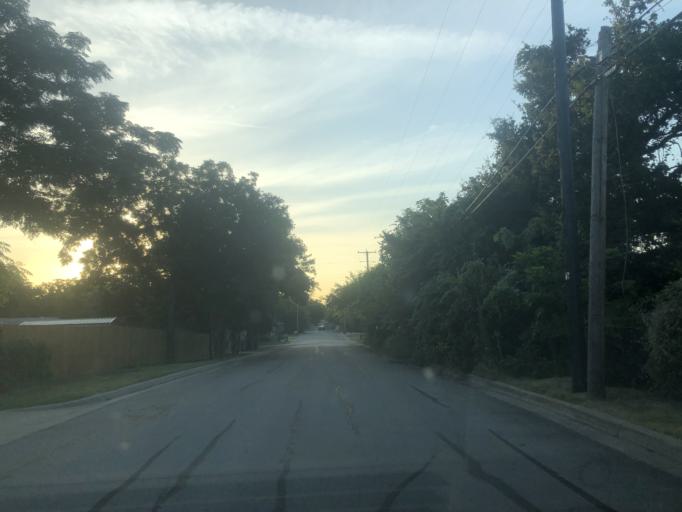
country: US
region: Texas
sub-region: Tarrant County
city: Lake Worth
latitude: 32.8021
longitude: -97.4491
